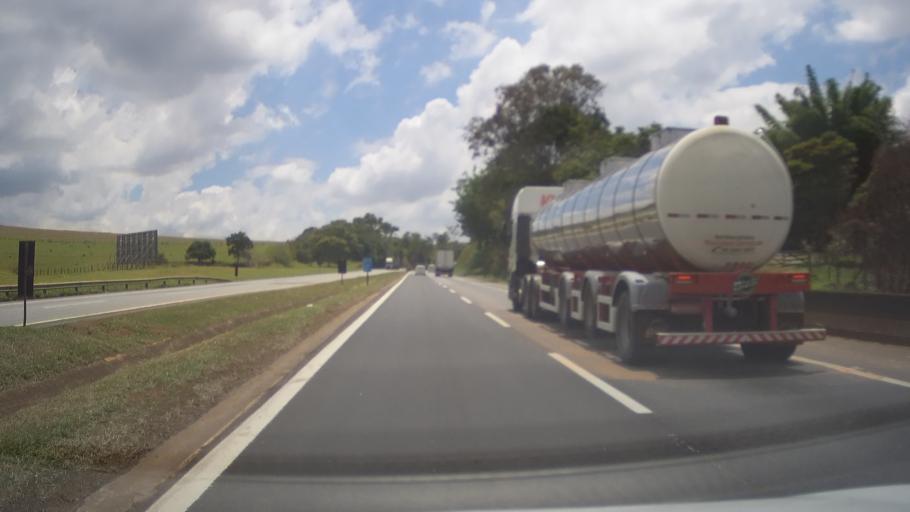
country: BR
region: Minas Gerais
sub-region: Tres Coracoes
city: Tres Coracoes
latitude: -21.7011
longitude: -45.3675
